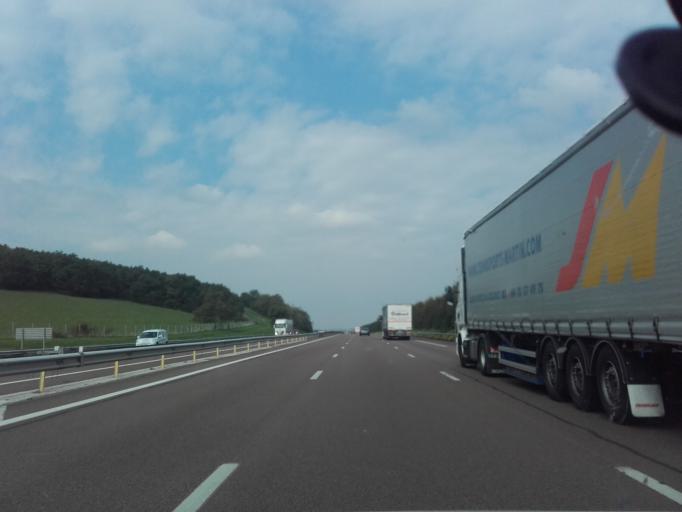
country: FR
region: Bourgogne
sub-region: Departement de Saone-et-Loire
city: Sennecey-le-Grand
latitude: 46.6394
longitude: 4.8594
